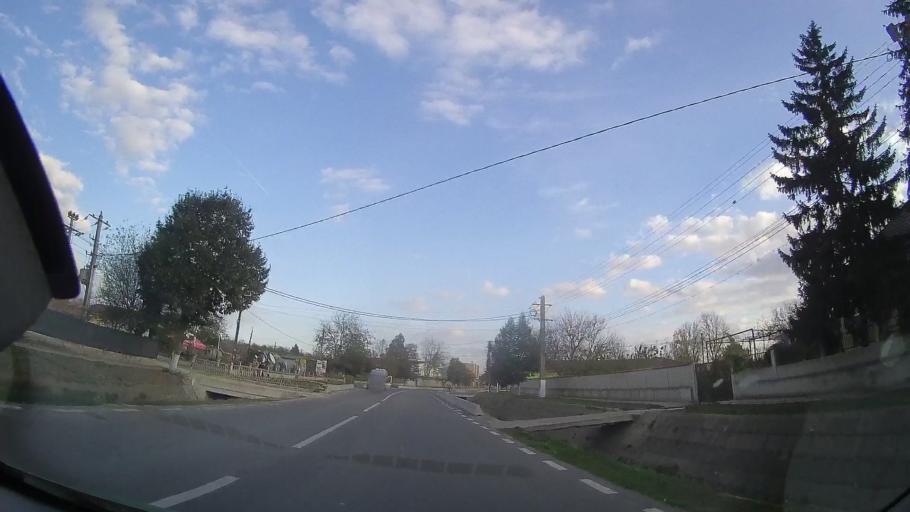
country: RO
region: Constanta
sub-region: Comuna Independenta
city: Independenta
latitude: 43.9516
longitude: 28.0824
